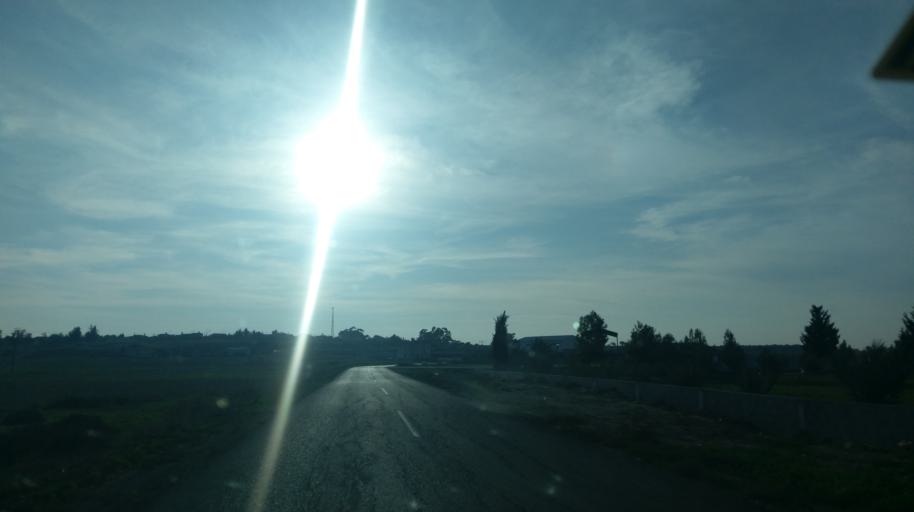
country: CY
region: Ammochostos
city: Achna
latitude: 35.0998
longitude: 33.8046
